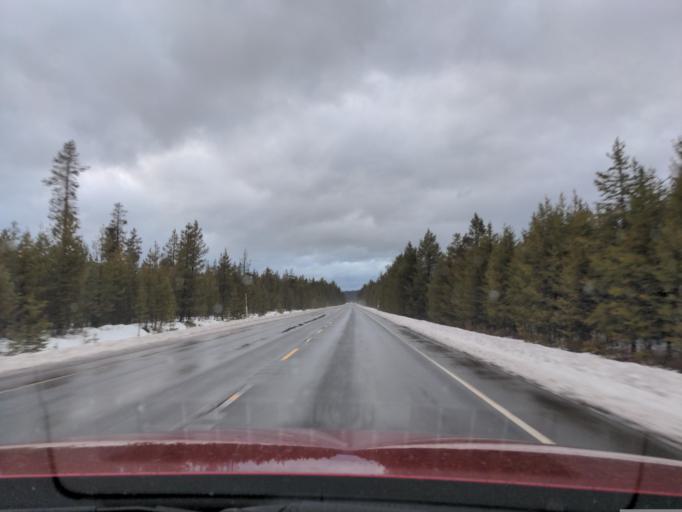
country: US
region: Oregon
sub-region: Deschutes County
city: La Pine
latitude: 43.4067
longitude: -121.8272
